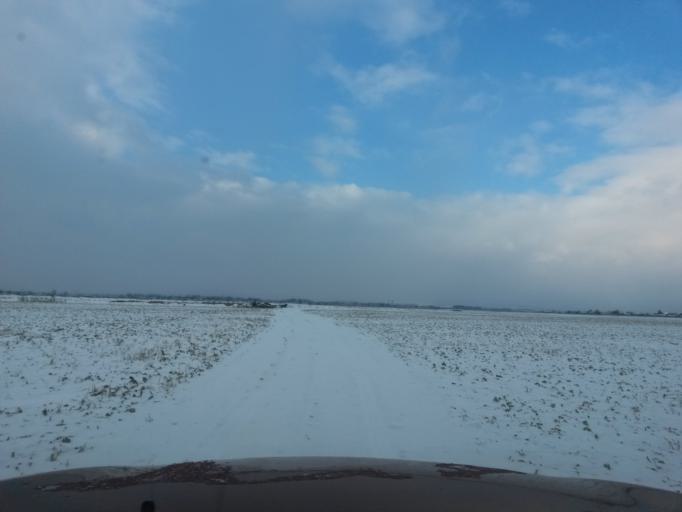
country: SK
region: Kosicky
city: Kosice
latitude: 48.6321
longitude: 21.3407
